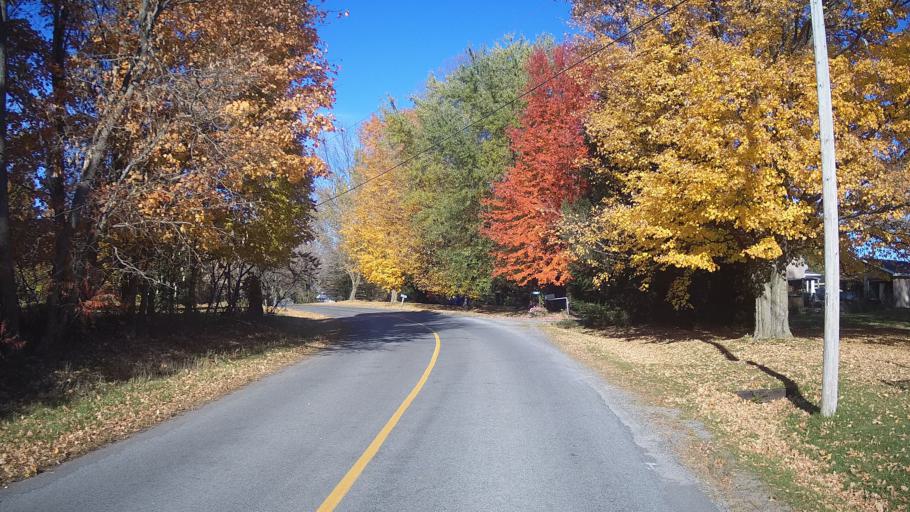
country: CA
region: Ontario
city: Kingston
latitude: 44.4460
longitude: -76.5178
